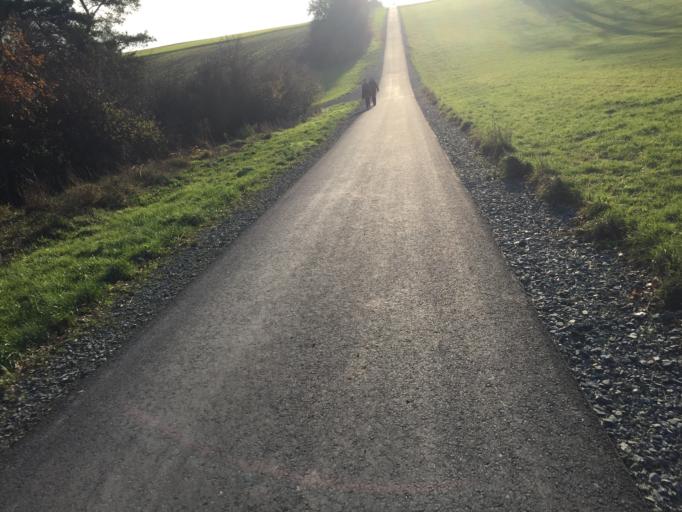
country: DE
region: Hesse
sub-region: Regierungsbezirk Giessen
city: Langgons
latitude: 50.5169
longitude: 8.7129
